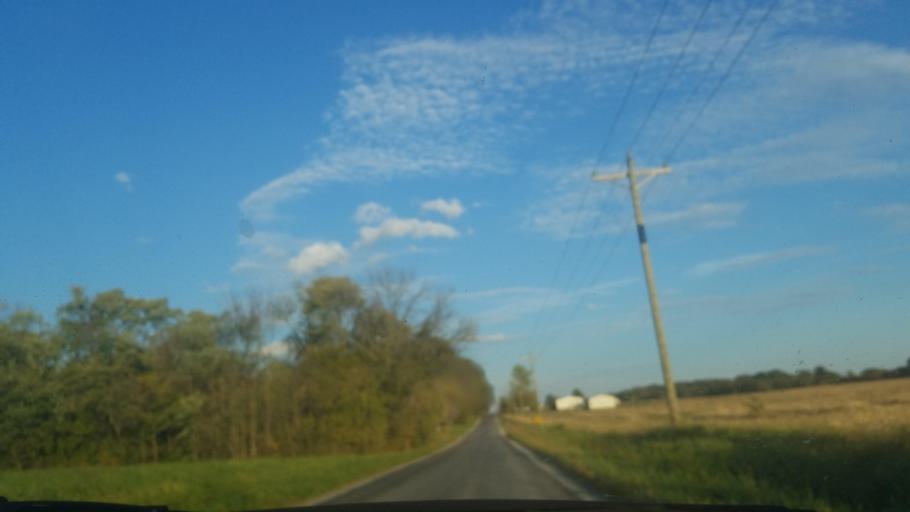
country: US
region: Illinois
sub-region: Saline County
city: Carrier Mills
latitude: 37.8050
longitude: -88.6504
